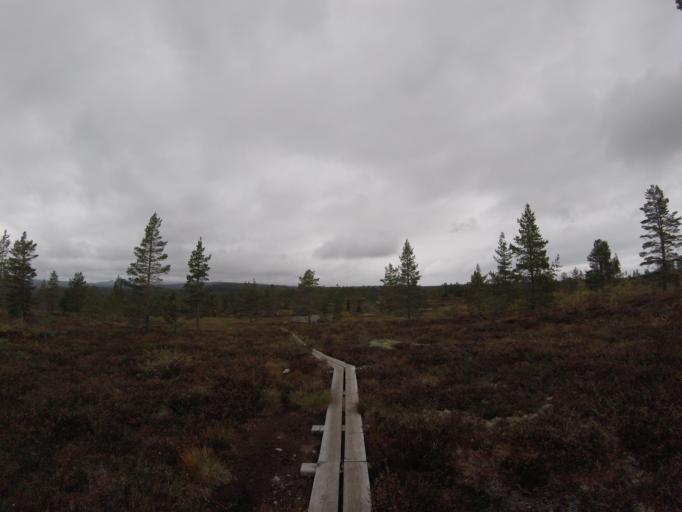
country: NO
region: Buskerud
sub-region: Flesberg
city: Lampeland
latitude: 59.7579
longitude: 9.4018
